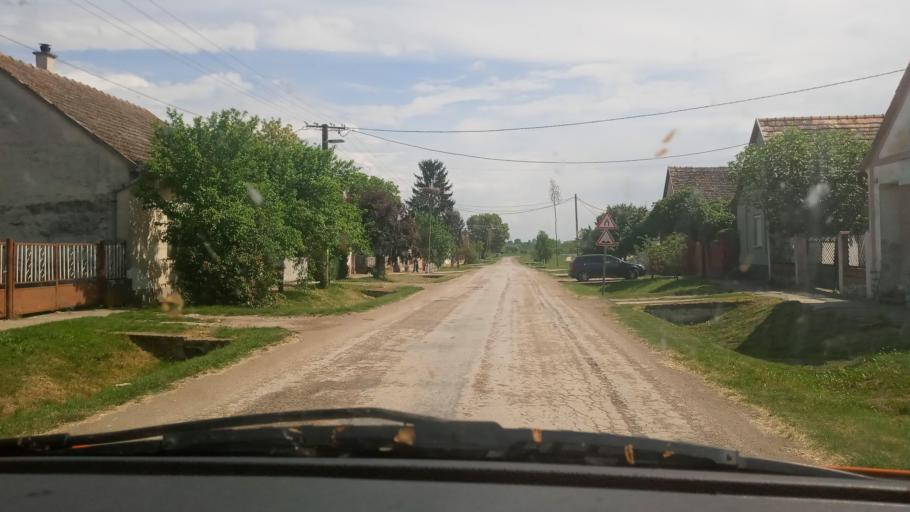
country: HU
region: Baranya
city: Beremend
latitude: 45.7874
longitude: 18.3536
